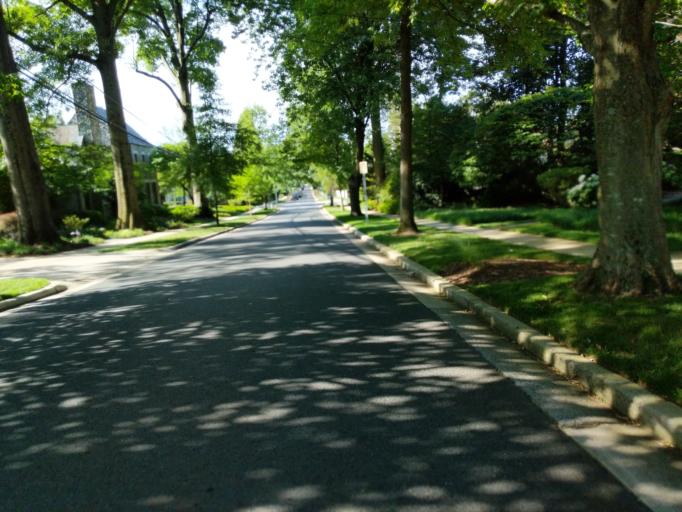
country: US
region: Maryland
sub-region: Montgomery County
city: Bethesda
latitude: 38.9854
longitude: -77.1033
